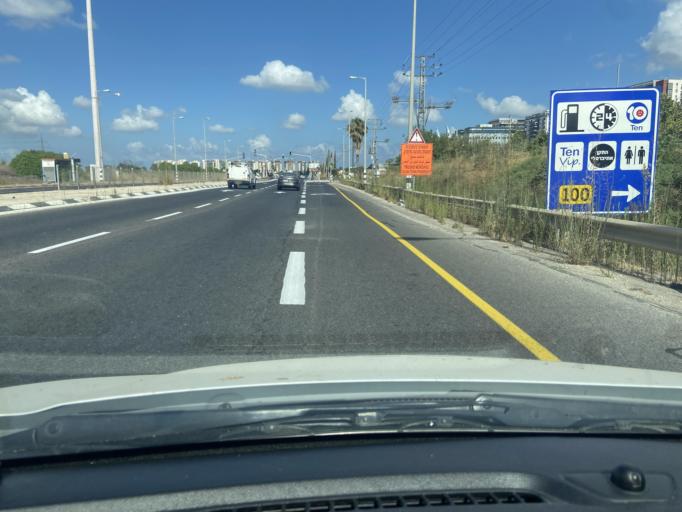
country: IL
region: Central District
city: Yehud
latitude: 32.0265
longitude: 34.8927
